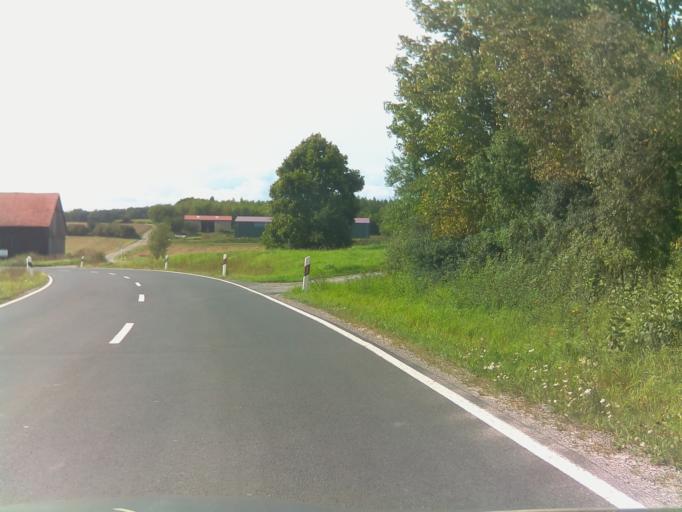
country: DE
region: Bavaria
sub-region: Regierungsbezirk Unterfranken
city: Arnstein
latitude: 49.9296
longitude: 9.9671
